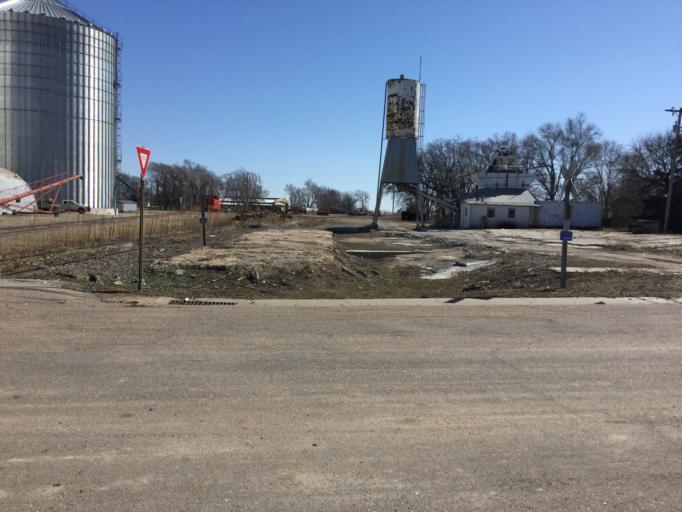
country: US
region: Kansas
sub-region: Marshall County
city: Blue Rapids
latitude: 39.6747
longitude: -96.6609
